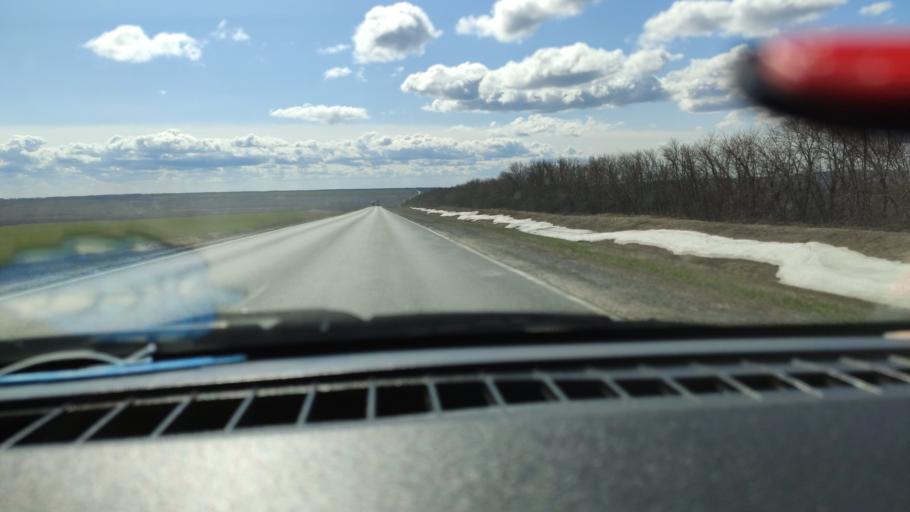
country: RU
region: Saratov
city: Dukhovnitskoye
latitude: 52.7582
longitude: 48.2432
